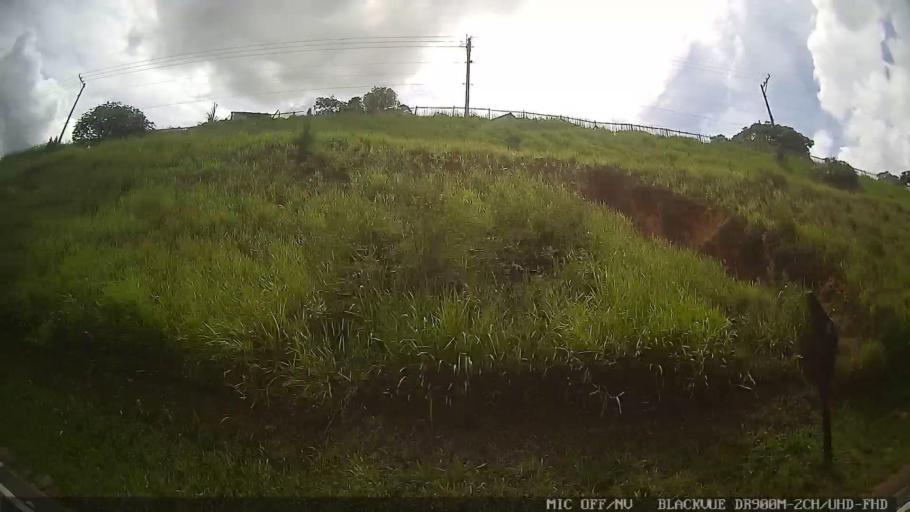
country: BR
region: Sao Paulo
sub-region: Suzano
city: Suzano
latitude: -23.6041
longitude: -46.3107
